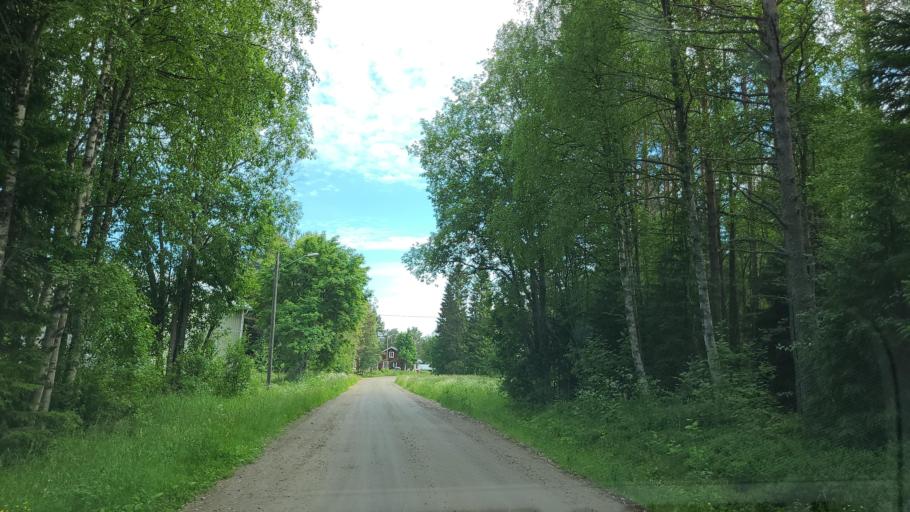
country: SE
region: Vaesterbotten
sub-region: Robertsfors Kommun
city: Robertsfors
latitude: 64.1641
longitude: 20.9625
